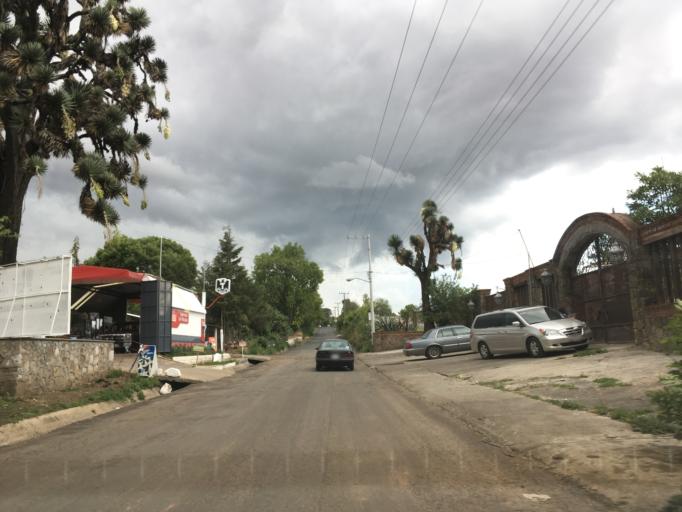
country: MX
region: Michoacan
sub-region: Morelia
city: La Mintzita (Piedra Dura)
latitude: 19.5879
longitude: -101.2737
